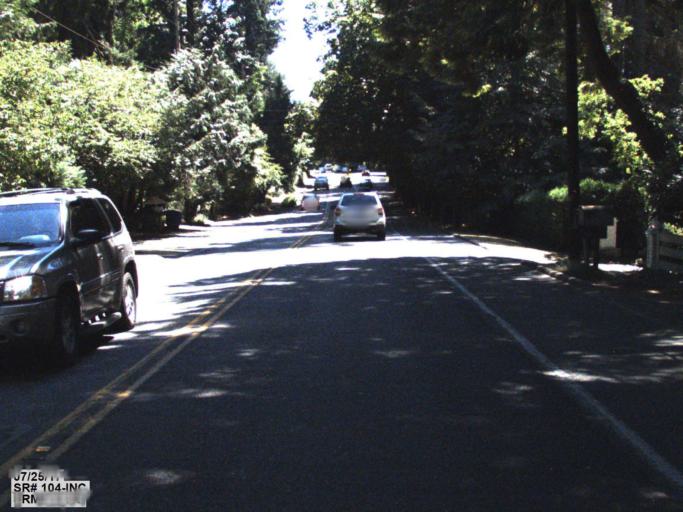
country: US
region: Washington
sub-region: King County
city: Lake Forest Park
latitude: 47.7583
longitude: -122.2822
